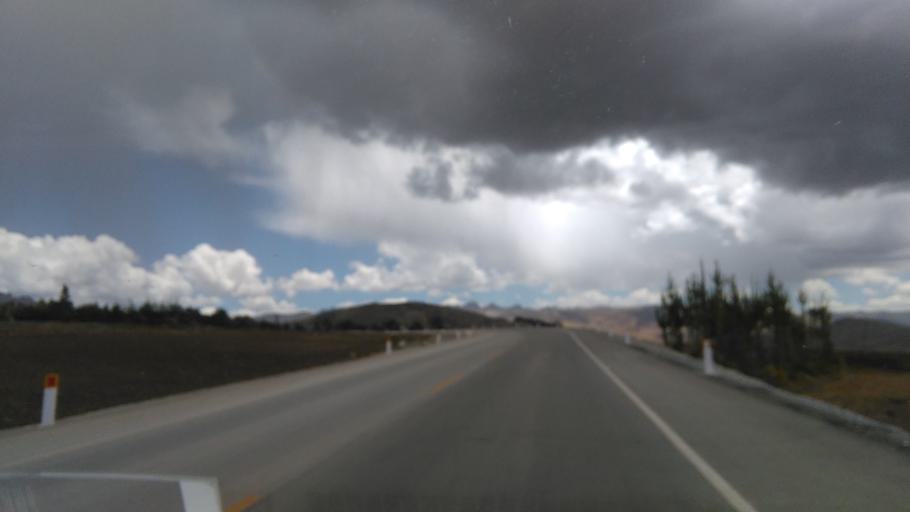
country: PE
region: Apurimac
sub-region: Provincia de Andahuaylas
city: San Jeronimo
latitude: -13.7249
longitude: -73.3516
